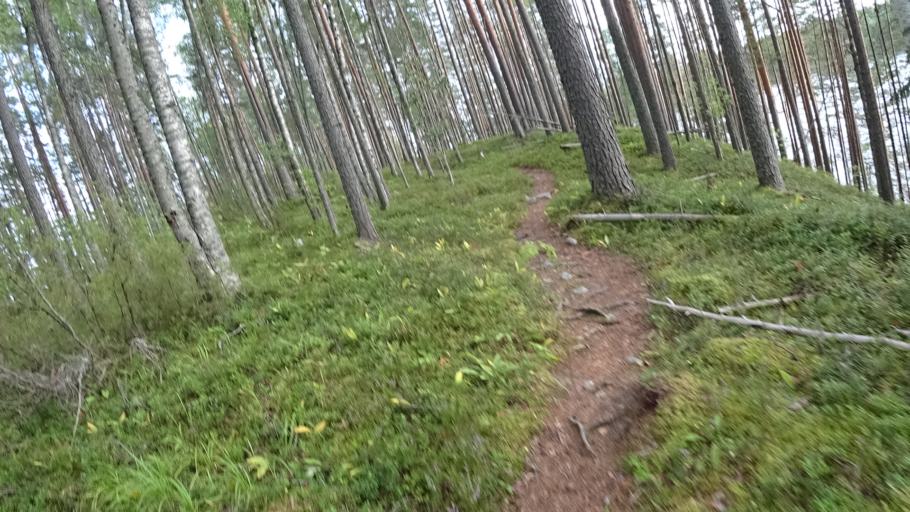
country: FI
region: North Karelia
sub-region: Joensuu
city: Ilomantsi
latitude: 62.5722
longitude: 31.1760
